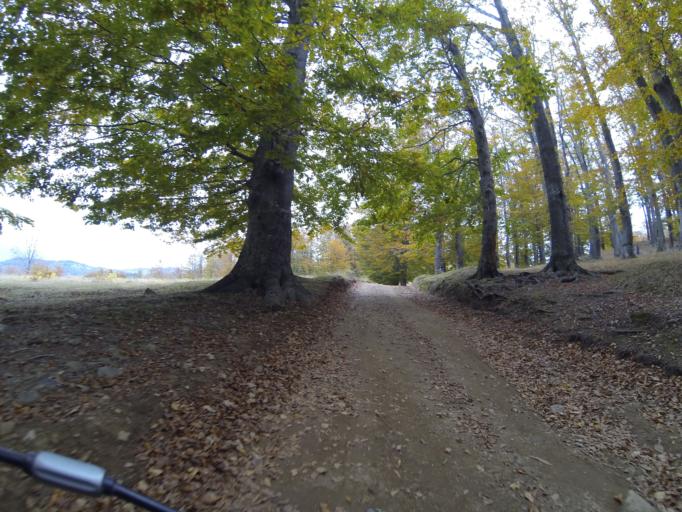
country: RO
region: Gorj
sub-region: Comuna Tismana
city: Sohodol
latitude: 45.1239
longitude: 22.8592
